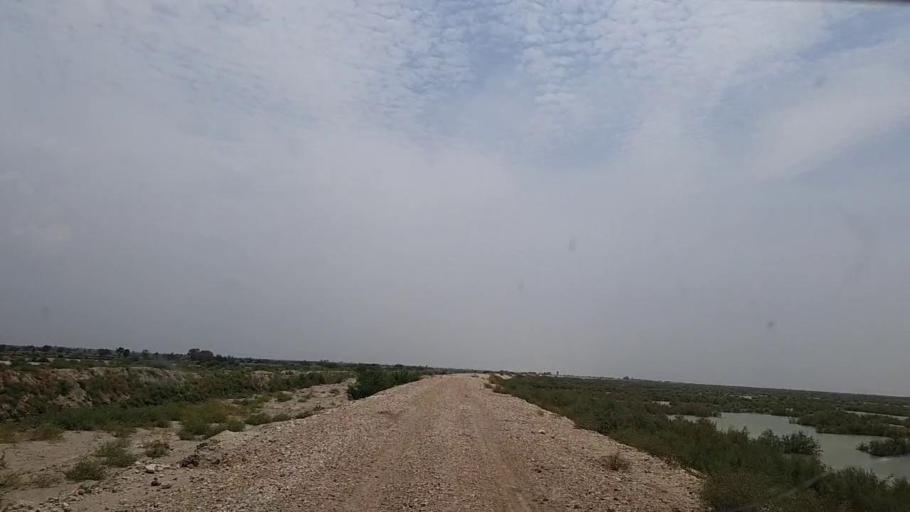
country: PK
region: Sindh
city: Phulji
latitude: 26.8714
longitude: 67.6486
